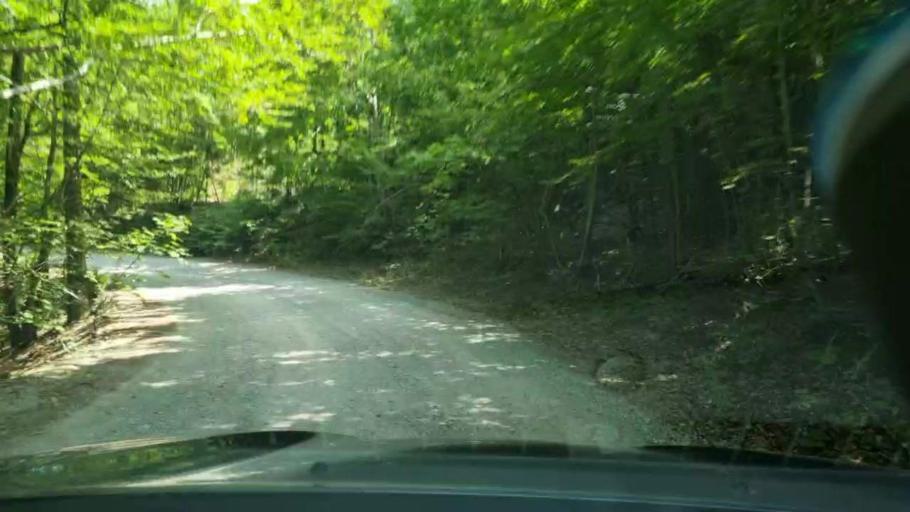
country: BA
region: Federation of Bosnia and Herzegovina
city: Bosansko Grahovo
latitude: 44.3004
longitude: 16.2621
